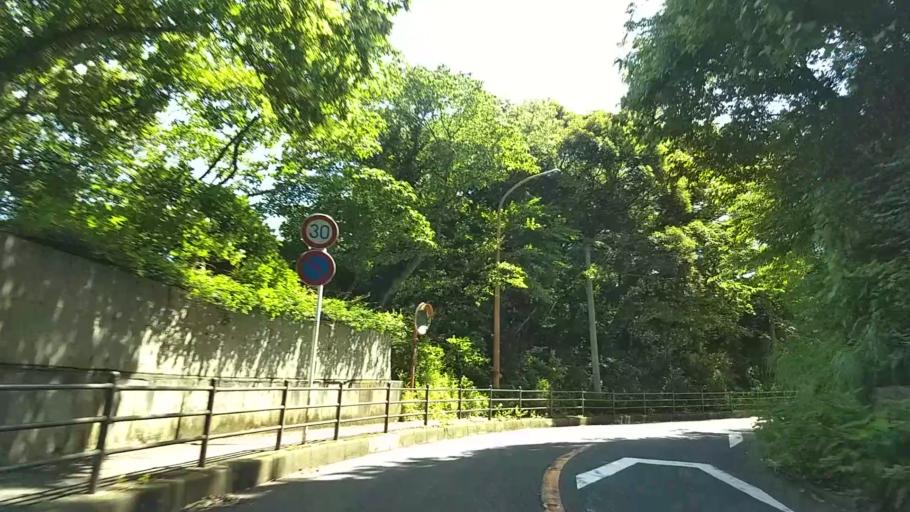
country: JP
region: Kanagawa
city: Zushi
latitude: 35.2943
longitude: 139.5911
